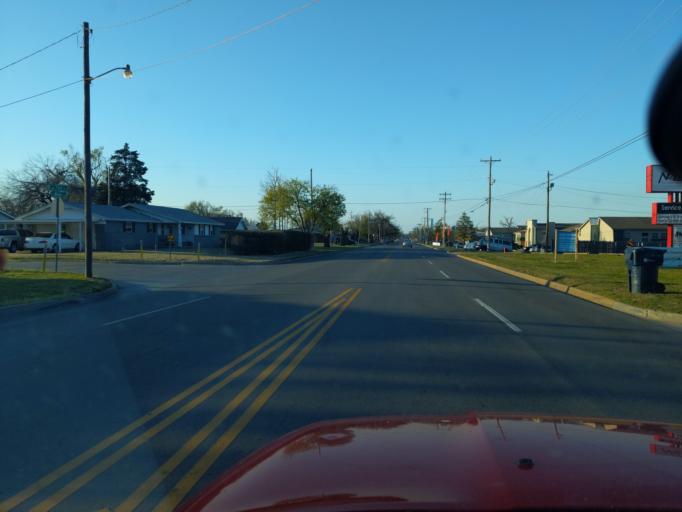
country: US
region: Oklahoma
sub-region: Cleveland County
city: Moore
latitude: 35.3948
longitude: -97.5216
